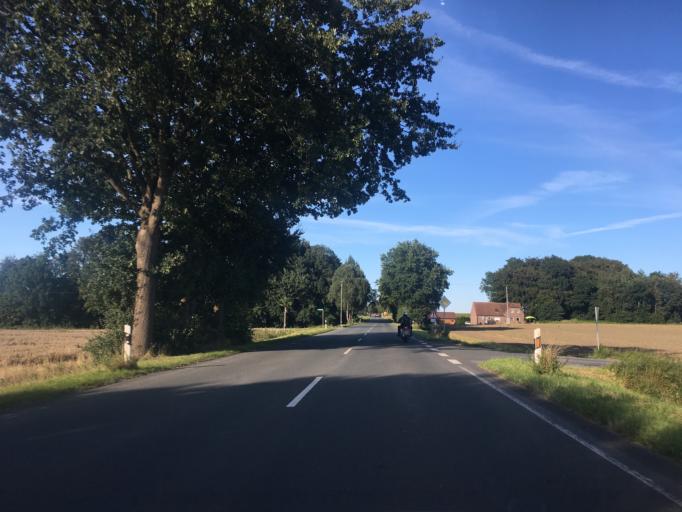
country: DE
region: North Rhine-Westphalia
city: Olfen
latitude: 51.7778
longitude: 7.3525
